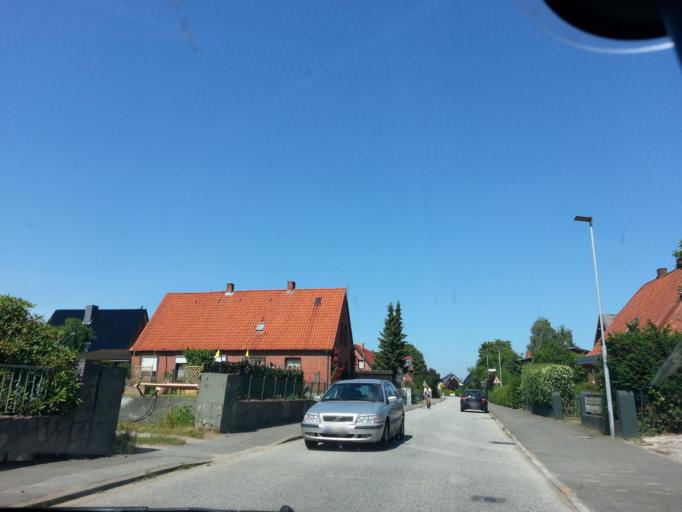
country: DE
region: Schleswig-Holstein
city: Breitenfelde
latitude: 53.6076
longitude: 10.6396
